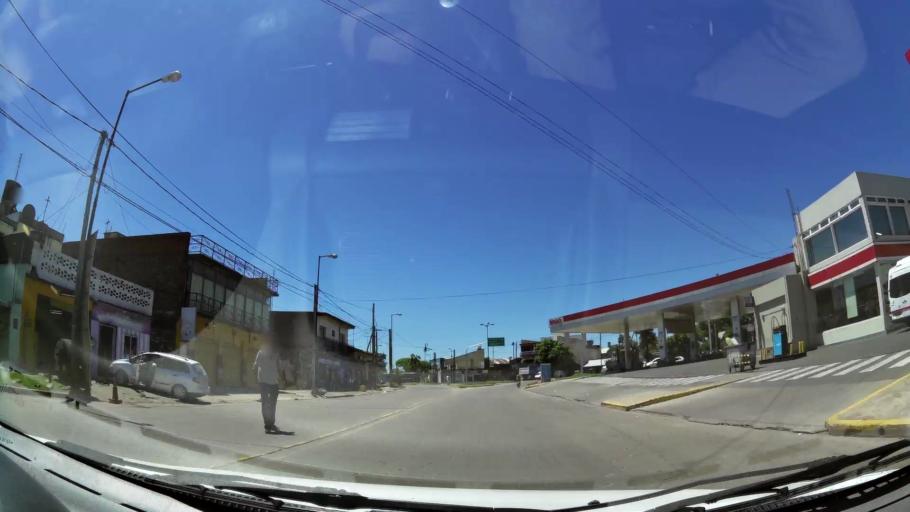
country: AR
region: Buenos Aires
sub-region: Partido de Tigre
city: Tigre
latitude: -34.4972
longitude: -58.5823
